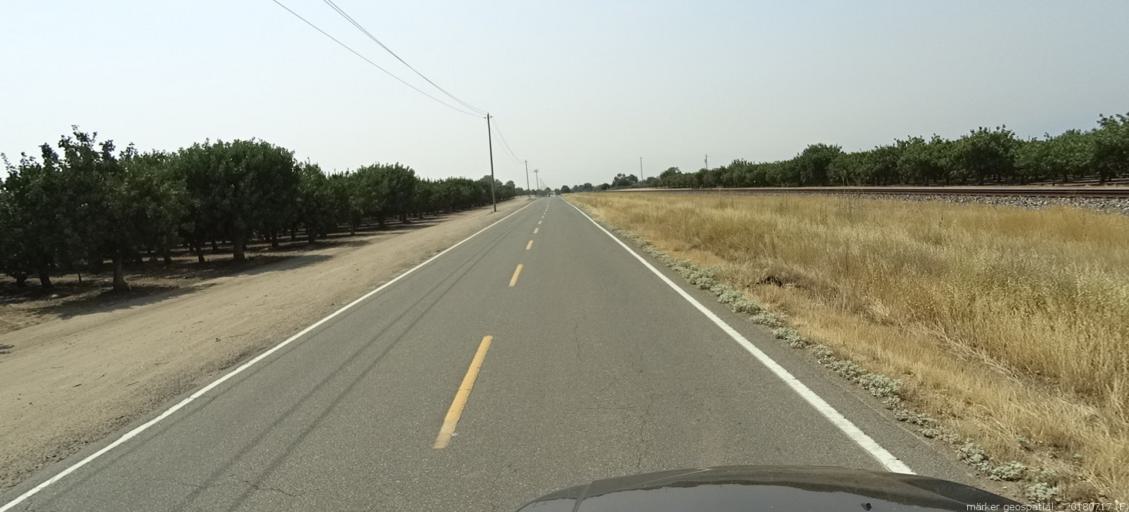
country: US
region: California
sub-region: Madera County
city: Fairmead
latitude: 37.1509
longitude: -120.1668
